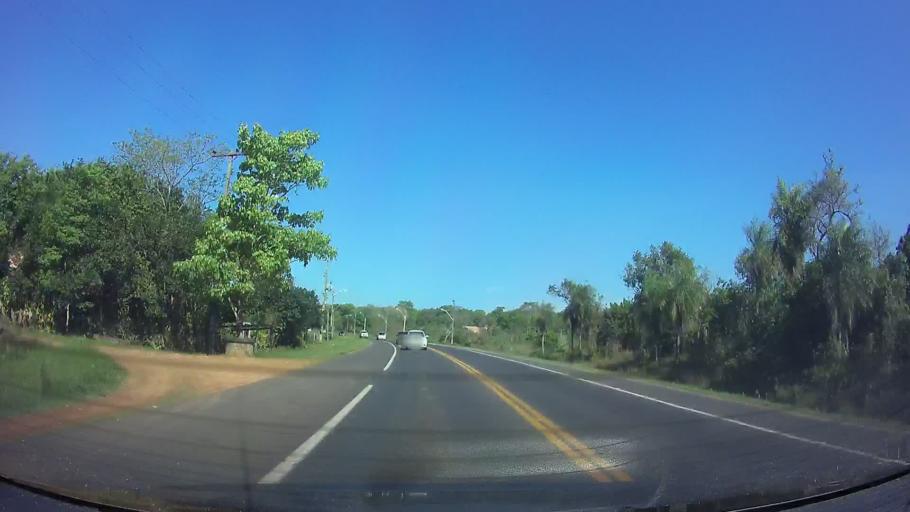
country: PY
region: Central
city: Itaugua
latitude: -25.3548
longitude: -57.3336
